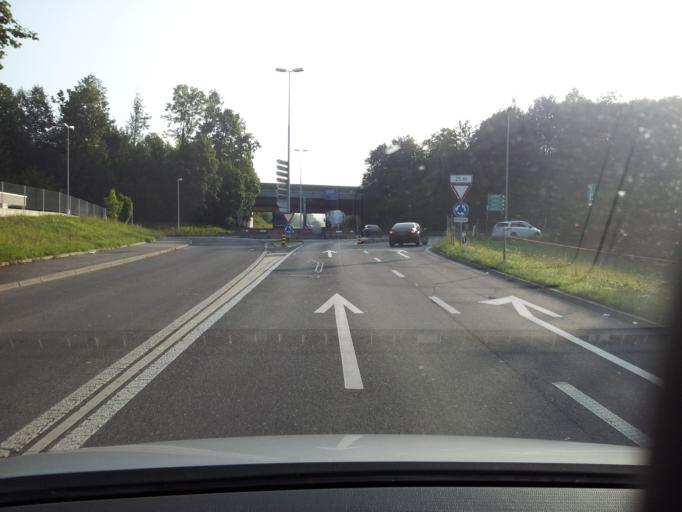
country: CH
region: Lucerne
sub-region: Sursee District
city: Sempach
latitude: 47.1361
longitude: 8.1976
